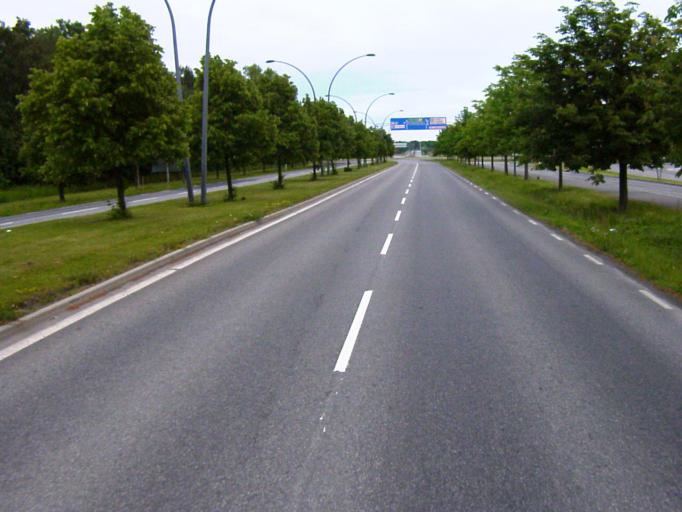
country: SE
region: Skane
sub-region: Kristianstads Kommun
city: Kristianstad
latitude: 56.0260
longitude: 14.1709
